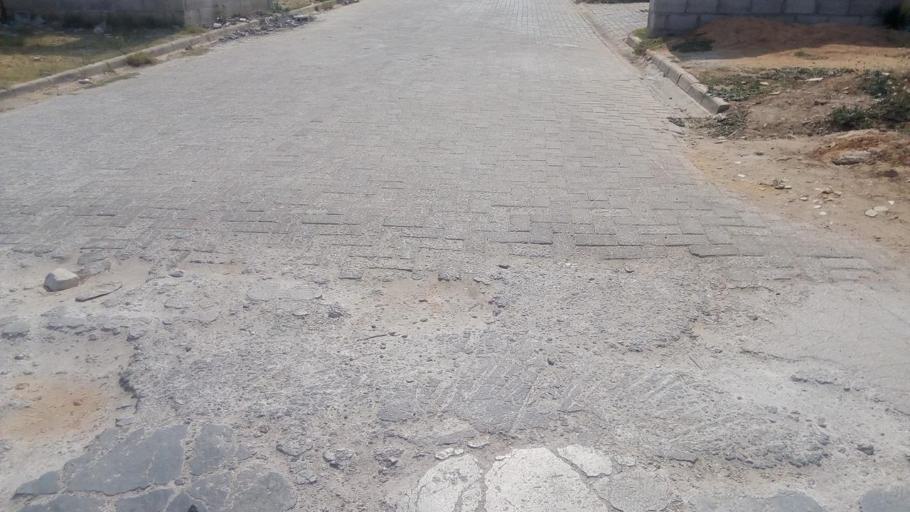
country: ZM
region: Lusaka
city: Lusaka
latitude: -15.3614
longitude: 28.2795
